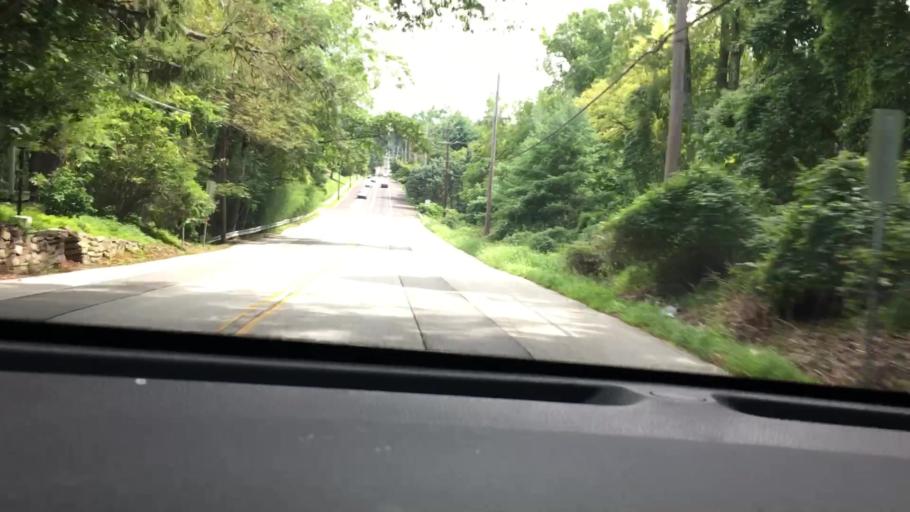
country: US
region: Pennsylvania
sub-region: Montgomery County
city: Bryn Athyn
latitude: 40.1389
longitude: -75.0410
